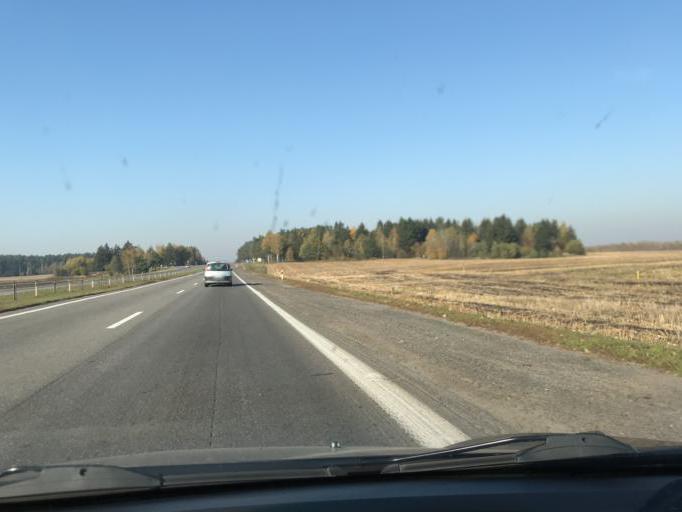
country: BY
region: Minsk
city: Dukora
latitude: 53.7085
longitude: 27.8753
